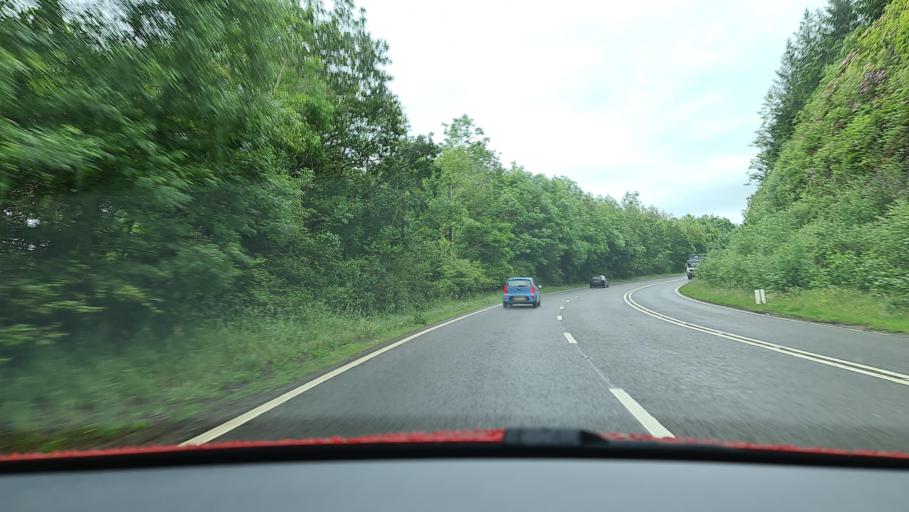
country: GB
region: England
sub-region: Cornwall
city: Liskeard
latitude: 50.4583
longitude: -4.5488
